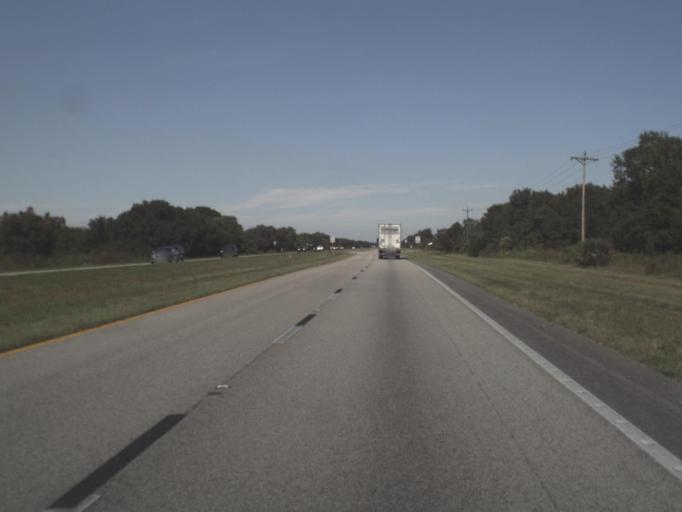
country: US
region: Florida
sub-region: Hendry County
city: Port LaBelle
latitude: 26.9484
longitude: -81.3164
